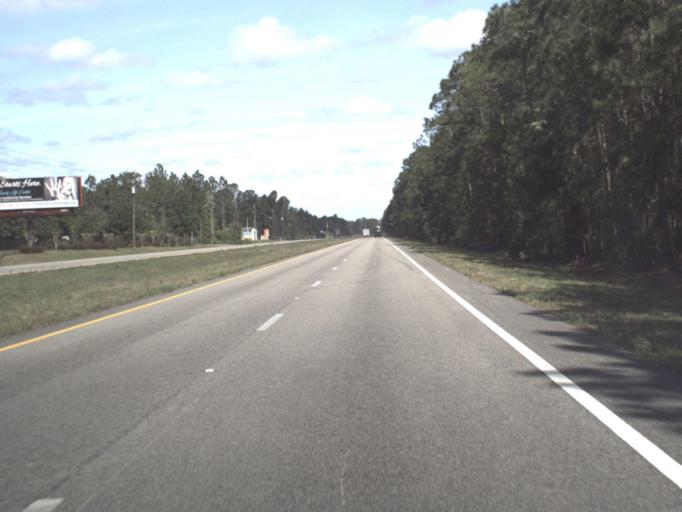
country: US
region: Florida
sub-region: Flagler County
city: Flagler Beach
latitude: 29.3761
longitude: -81.1803
